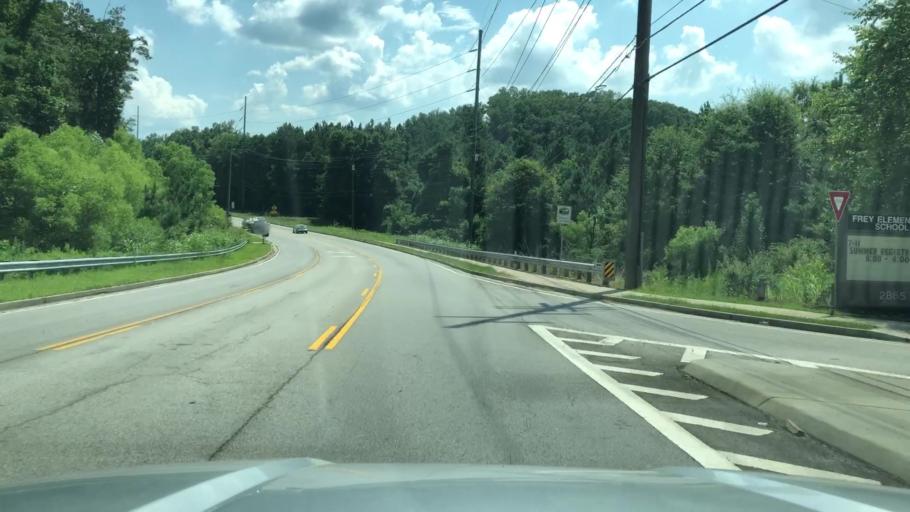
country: US
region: Georgia
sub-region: Cobb County
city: Acworth
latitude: 34.0242
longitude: -84.6989
